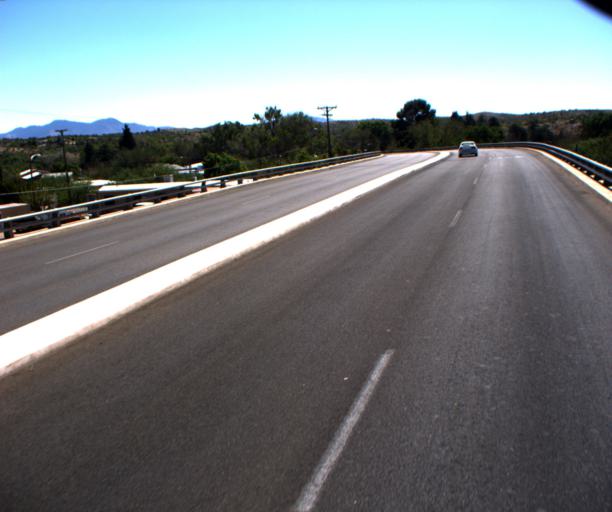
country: US
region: Arizona
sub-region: Santa Cruz County
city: Nogales
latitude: 31.3494
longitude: -110.9285
